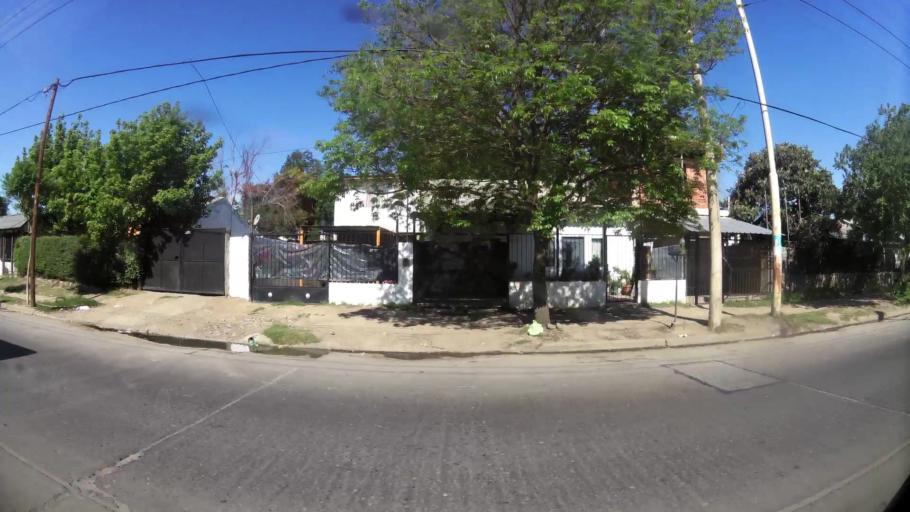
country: AR
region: Cordoba
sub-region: Departamento de Capital
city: Cordoba
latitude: -31.3767
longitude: -64.1838
